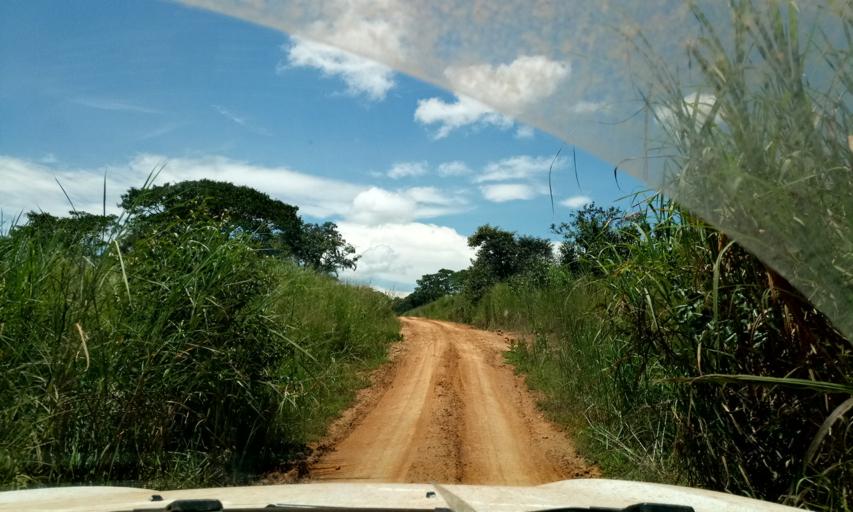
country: ZM
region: Northern
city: Kaputa
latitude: -7.8975
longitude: 29.1700
